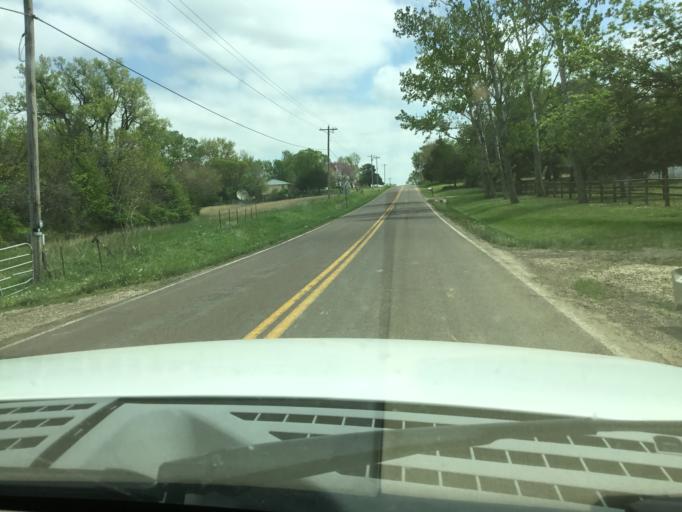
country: US
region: Kansas
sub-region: Shawnee County
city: Auburn
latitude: 38.9563
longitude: -95.8148
